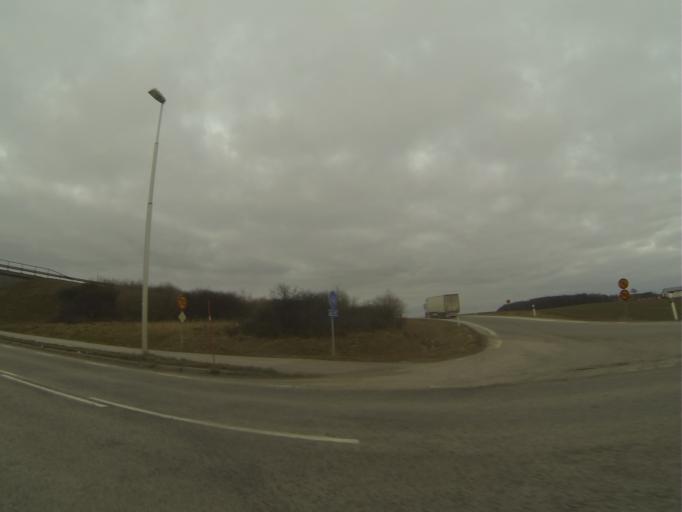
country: SE
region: Skane
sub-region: Skurups Kommun
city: Skurup
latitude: 55.4922
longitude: 13.4816
